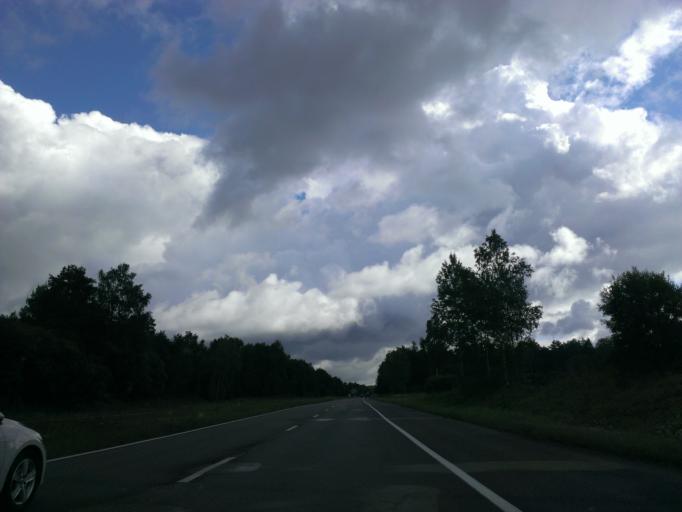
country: LV
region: Incukalns
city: Incukalns
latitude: 57.1255
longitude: 24.6919
